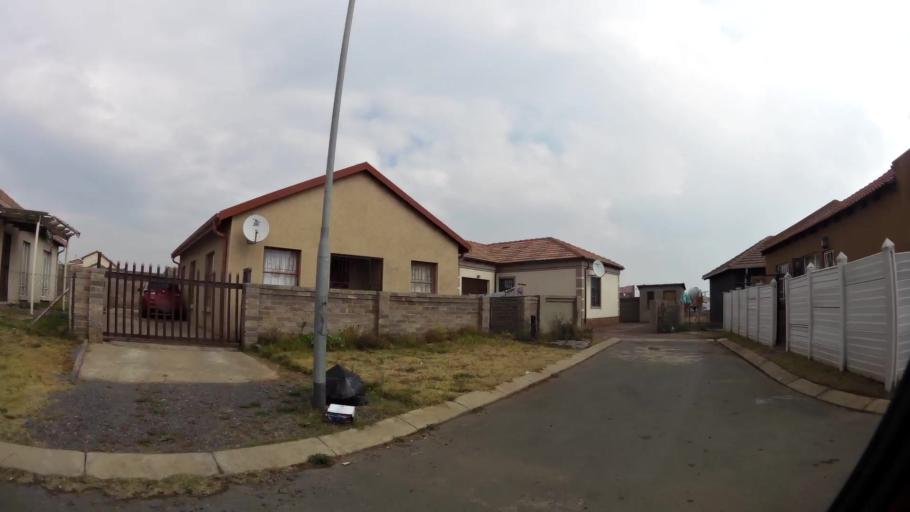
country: ZA
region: Gauteng
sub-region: Sedibeng District Municipality
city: Vanderbijlpark
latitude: -26.6829
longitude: 27.8499
